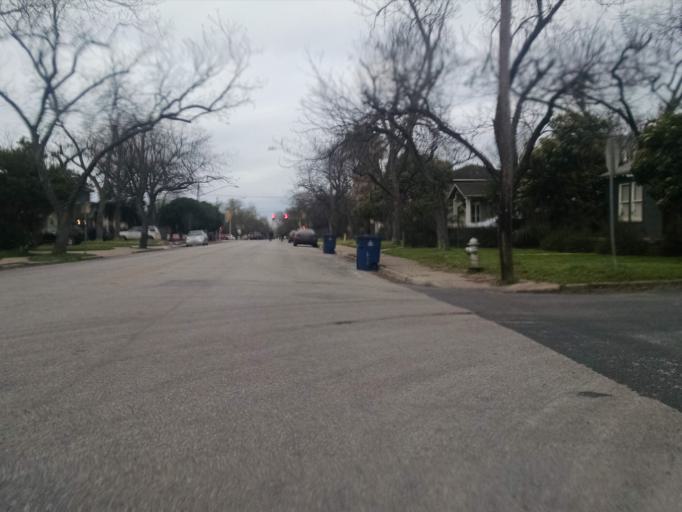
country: US
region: Texas
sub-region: Travis County
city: Austin
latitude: 30.3154
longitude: -97.7192
